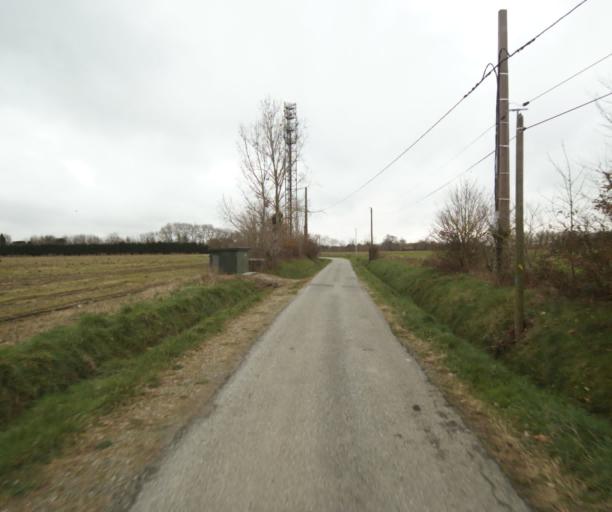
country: FR
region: Midi-Pyrenees
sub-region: Departement de l'Ariege
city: Mazeres
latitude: 43.2507
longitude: 1.6654
